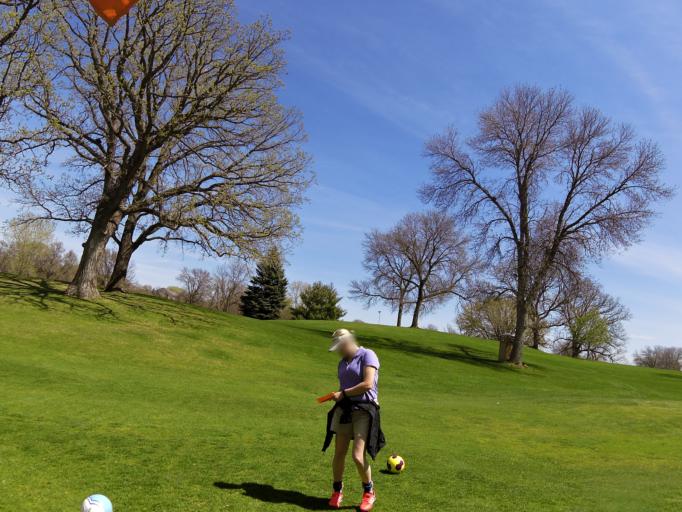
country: US
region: Minnesota
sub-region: Scott County
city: Savage
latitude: 44.8207
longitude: -93.3576
